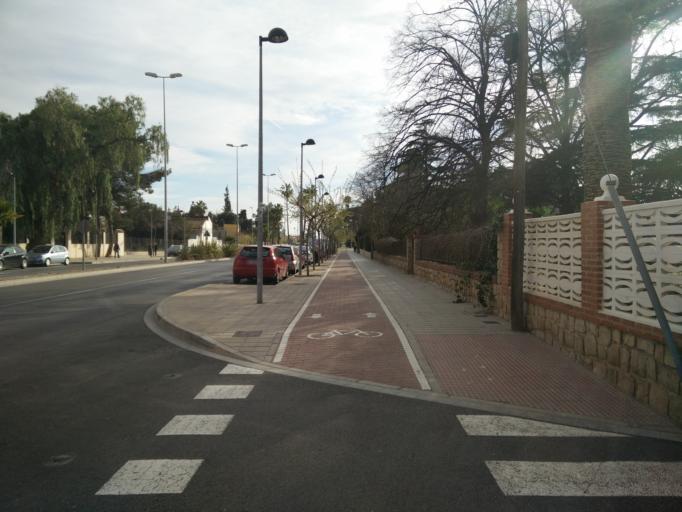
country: ES
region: Valencia
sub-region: Provincia de Castello
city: Castello de la Plana
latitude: 39.9836
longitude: -0.0513
